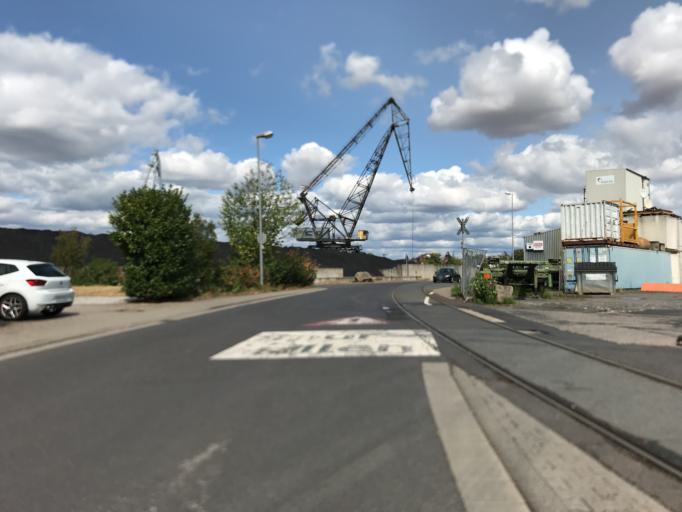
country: DE
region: Rheinland-Pfalz
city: Mainz
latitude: 49.9901
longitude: 8.3132
